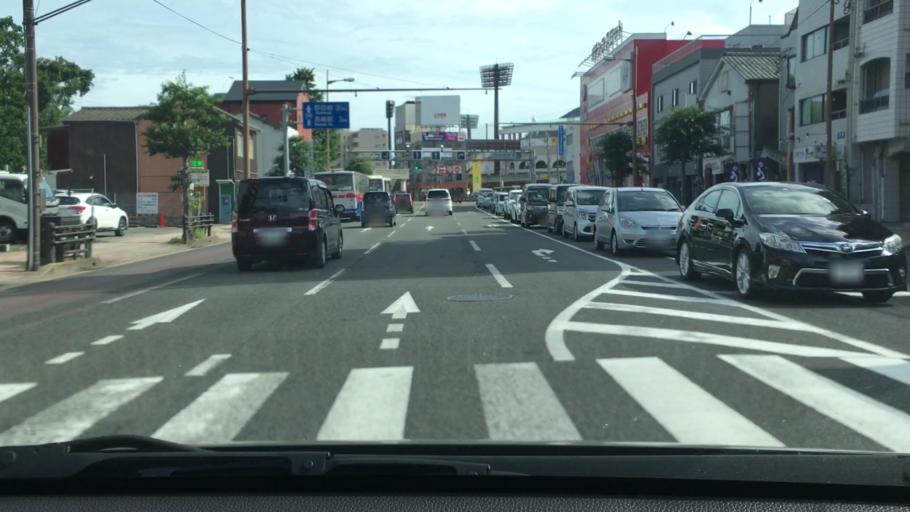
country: JP
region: Nagasaki
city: Nagasaki-shi
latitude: 32.7798
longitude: 129.8621
